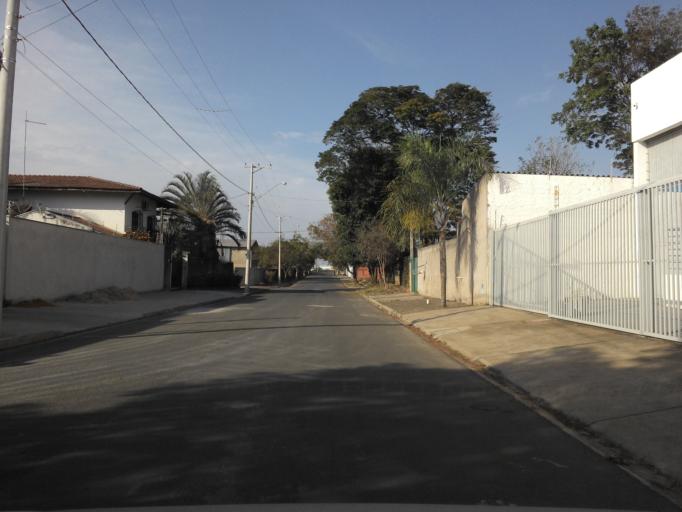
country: BR
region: Sao Paulo
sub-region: Hortolandia
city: Hortolandia
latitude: -22.9114
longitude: -47.2113
